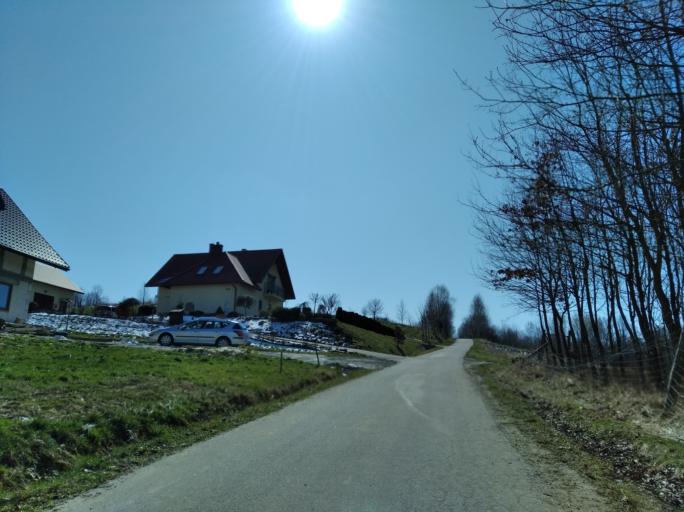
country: PL
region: Subcarpathian Voivodeship
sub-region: Powiat strzyzowski
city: Strzyzow
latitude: 49.8600
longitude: 21.8120
